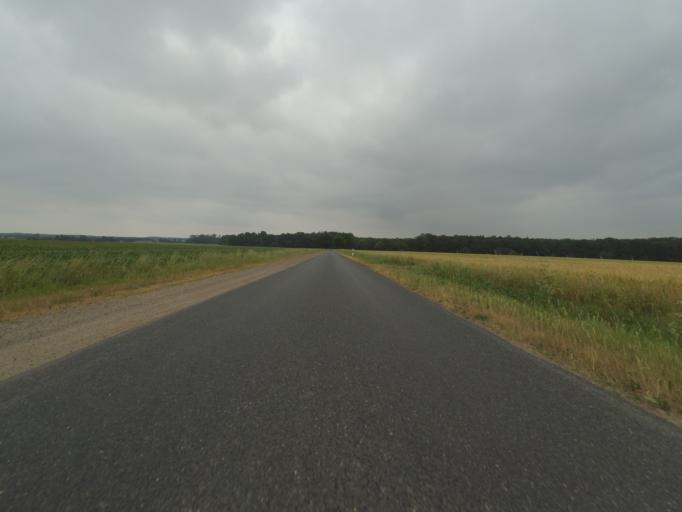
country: DE
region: Mecklenburg-Vorpommern
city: Spornitz
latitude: 53.3619
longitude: 11.6910
